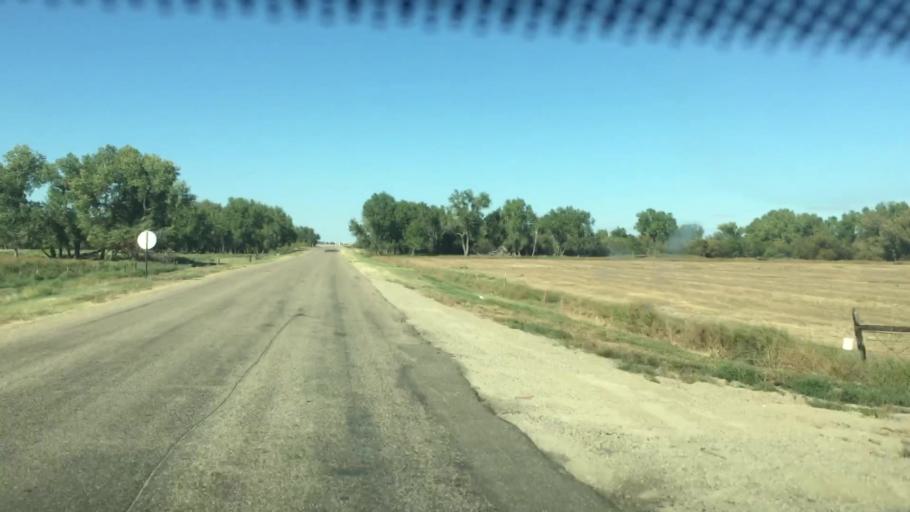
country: US
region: Colorado
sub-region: Prowers County
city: Lamar
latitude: 38.0933
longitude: -102.5196
